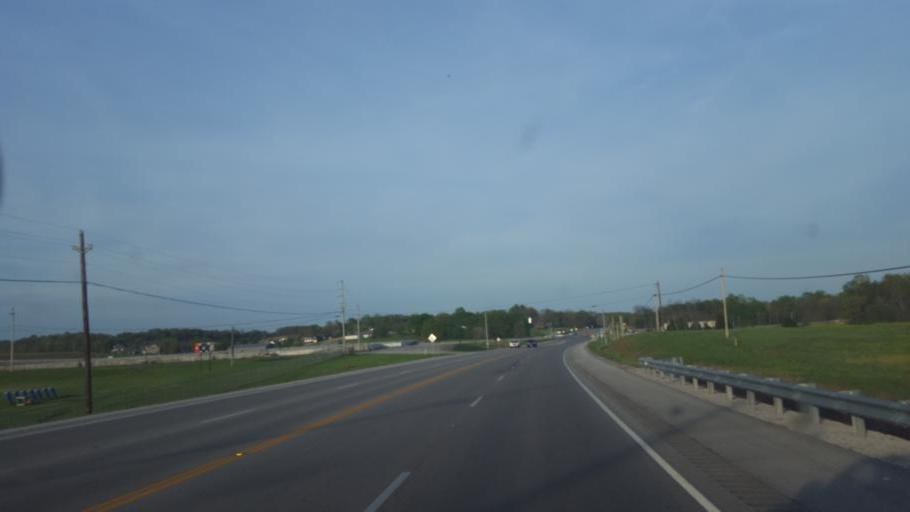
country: US
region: Kentucky
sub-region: Barren County
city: Glasgow
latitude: 37.0086
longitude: -85.8858
